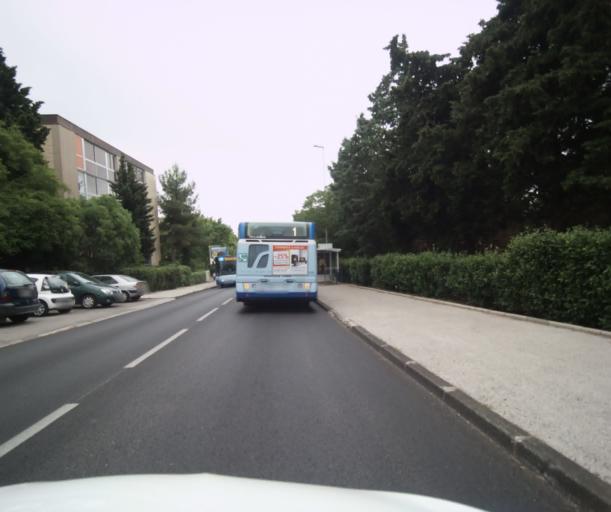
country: FR
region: Provence-Alpes-Cote d'Azur
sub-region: Departement du Var
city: La Seyne-sur-Mer
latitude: 43.1304
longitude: 5.8819
